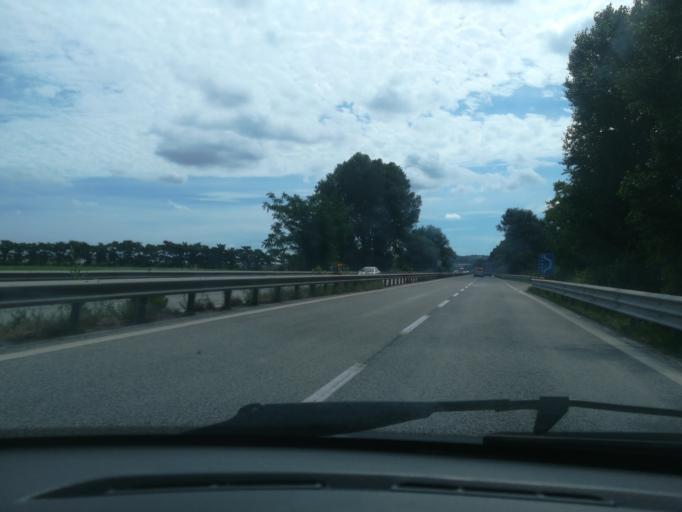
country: IT
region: The Marches
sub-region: Provincia di Macerata
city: Villa San Filippo
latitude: 43.2639
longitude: 13.5536
